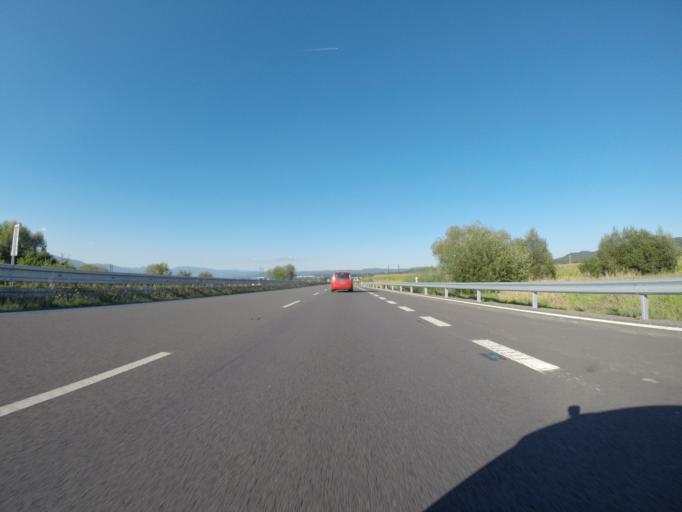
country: SK
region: Nitriansky
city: Prievidza
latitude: 48.7400
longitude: 18.6167
